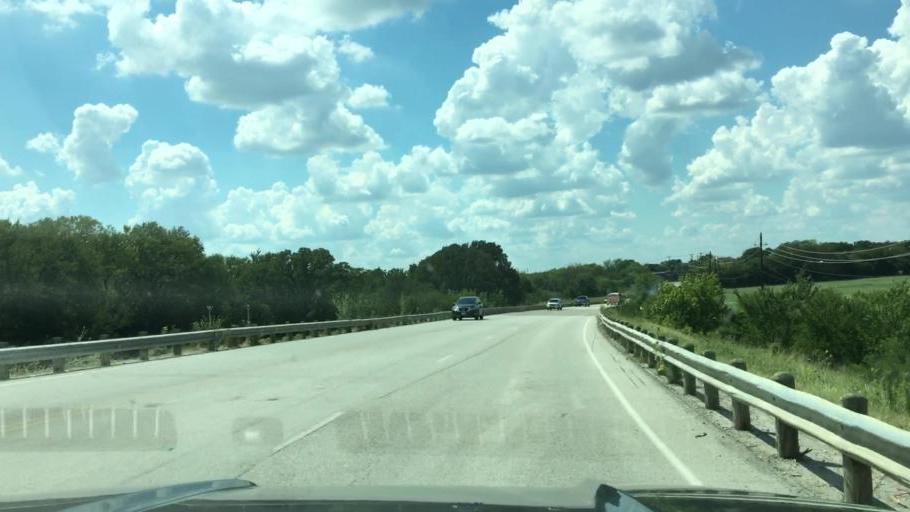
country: US
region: Texas
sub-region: Tarrant County
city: Haslet
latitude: 32.9743
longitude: -97.3425
